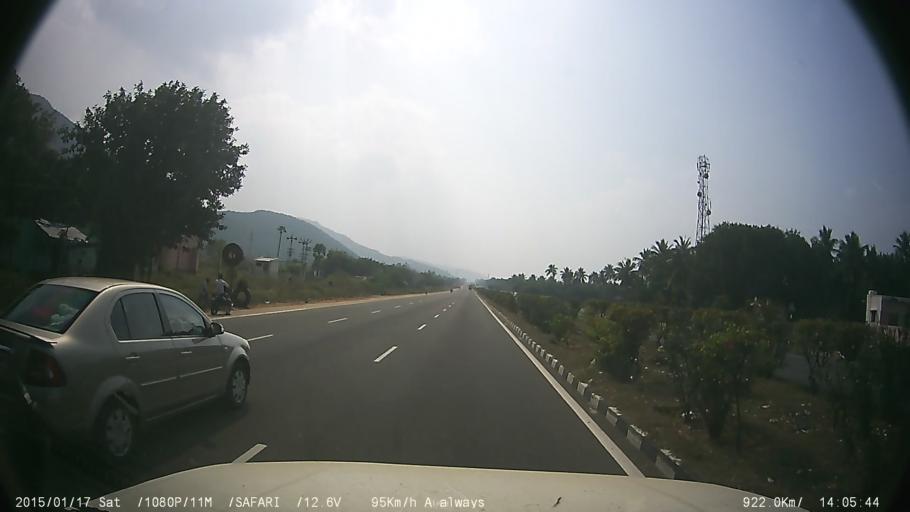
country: IN
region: Tamil Nadu
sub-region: Vellore
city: Ambur
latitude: 12.8457
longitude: 78.8030
